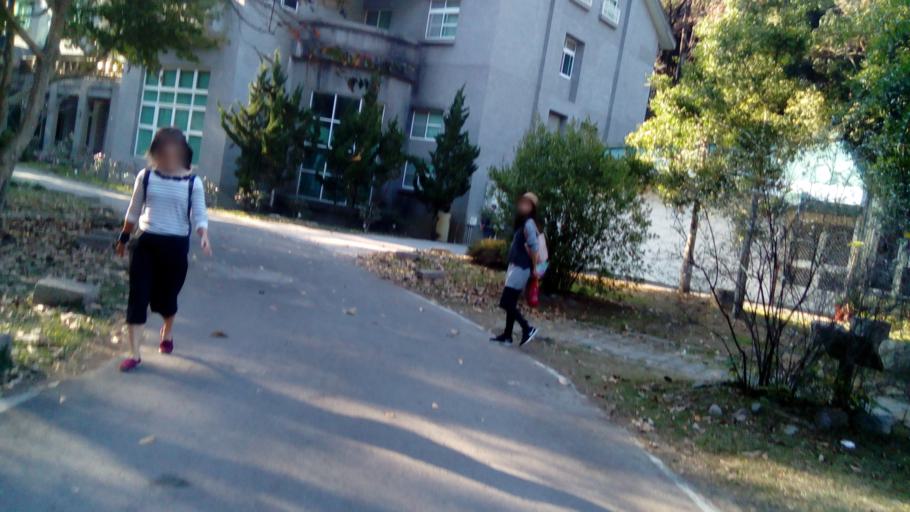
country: TW
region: Taiwan
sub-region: Nantou
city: Puli
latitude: 24.0908
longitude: 121.0319
